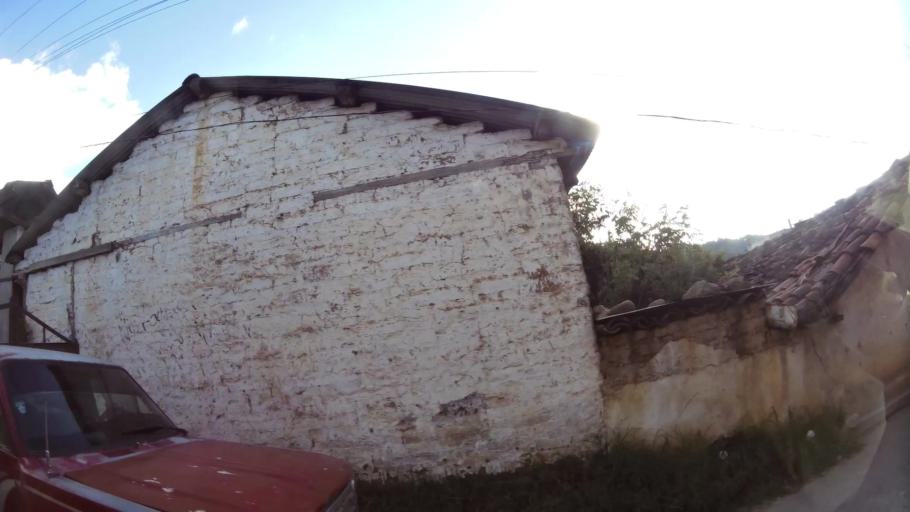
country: GT
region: Quiche
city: Chichicastenango
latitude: 14.9431
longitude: -91.1140
